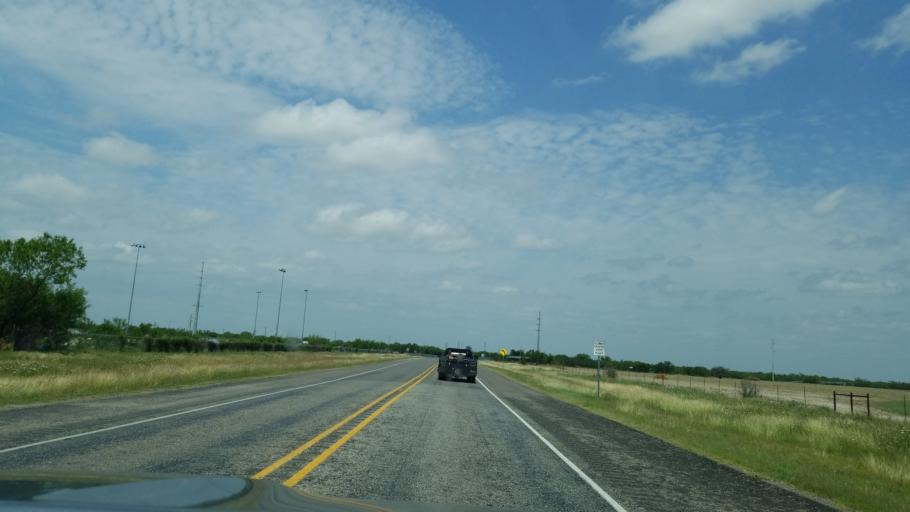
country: US
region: Texas
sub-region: Zavala County
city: La Pryor
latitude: 28.9438
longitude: -99.8302
